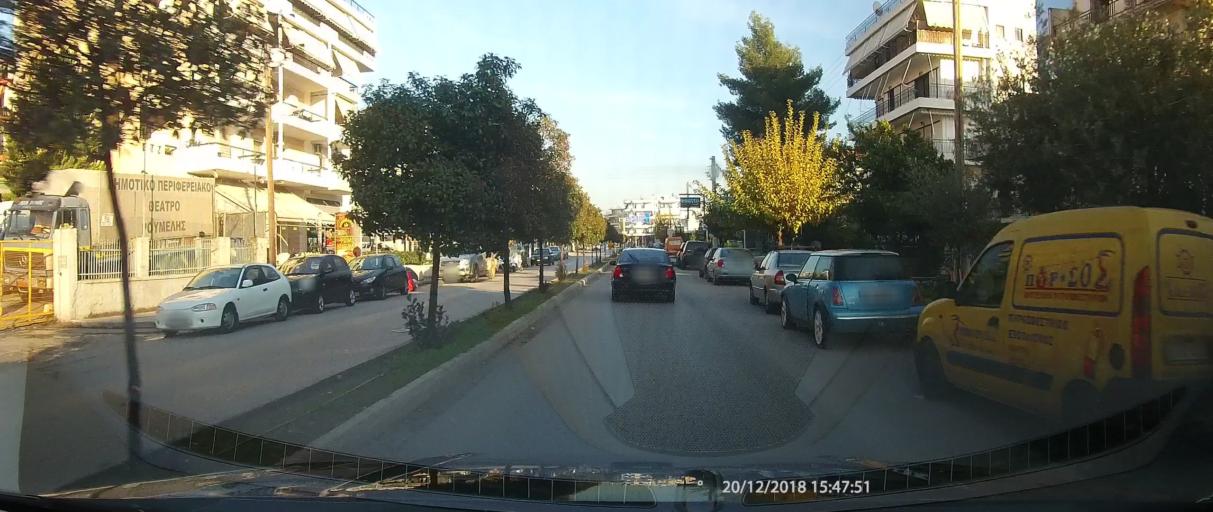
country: GR
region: Central Greece
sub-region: Nomos Fthiotidos
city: Lamia
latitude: 38.8936
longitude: 22.4360
